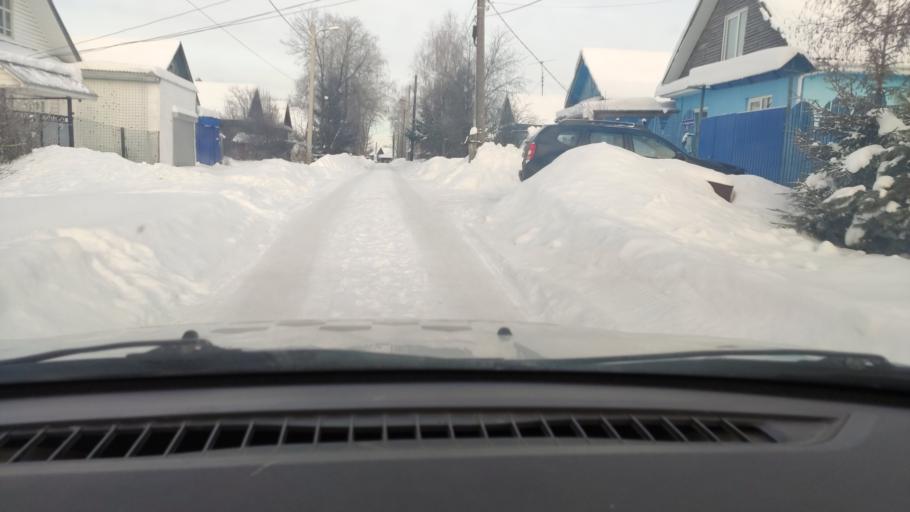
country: RU
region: Perm
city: Perm
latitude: 58.0420
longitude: 56.3572
